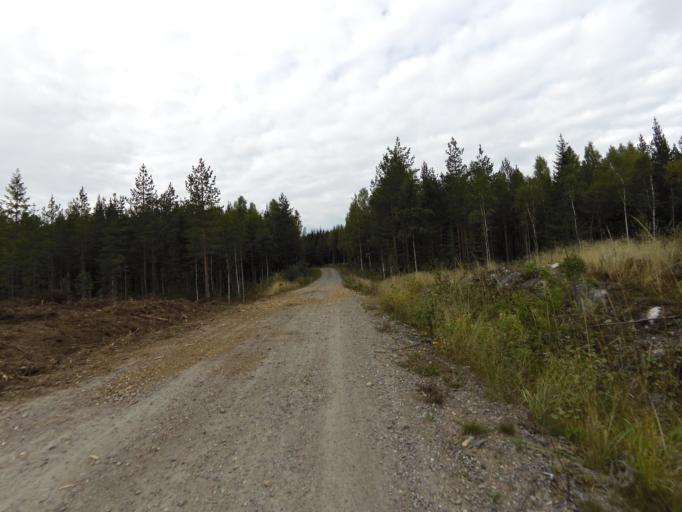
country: SE
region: Gaevleborg
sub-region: Gavle Kommun
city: Valbo
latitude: 60.7281
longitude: 17.0674
